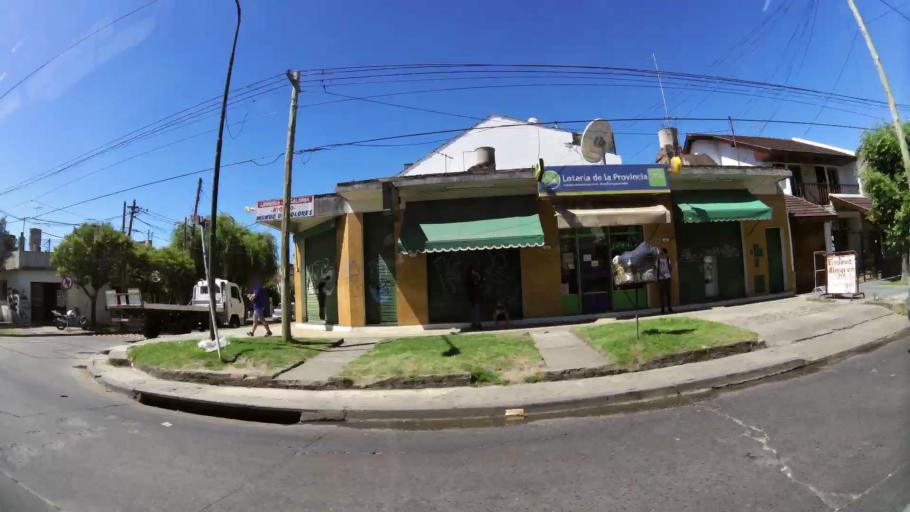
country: AR
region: Buenos Aires
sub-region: Partido de General San Martin
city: General San Martin
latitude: -34.5133
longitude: -58.5734
